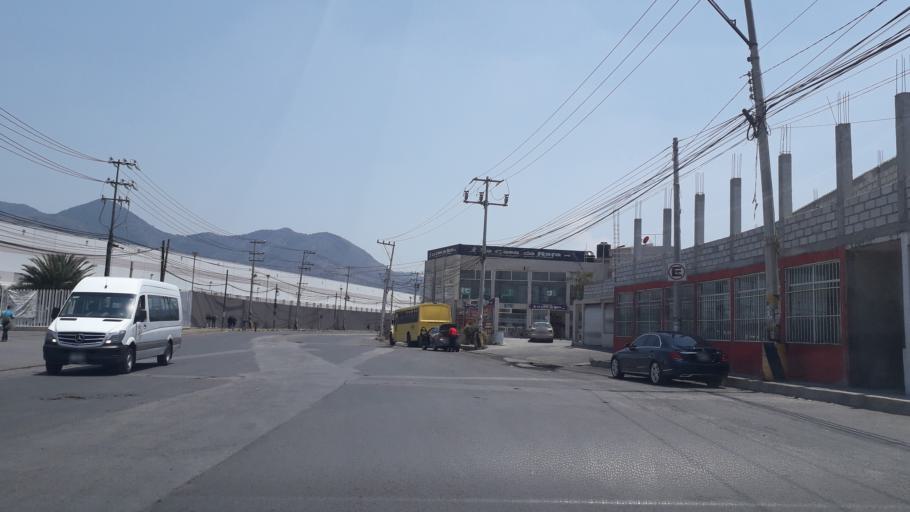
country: MX
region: Mexico
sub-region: Tultitlan
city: Colonia Lazaro Cardenas (Los Hornos)
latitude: 19.6285
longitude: -99.1529
